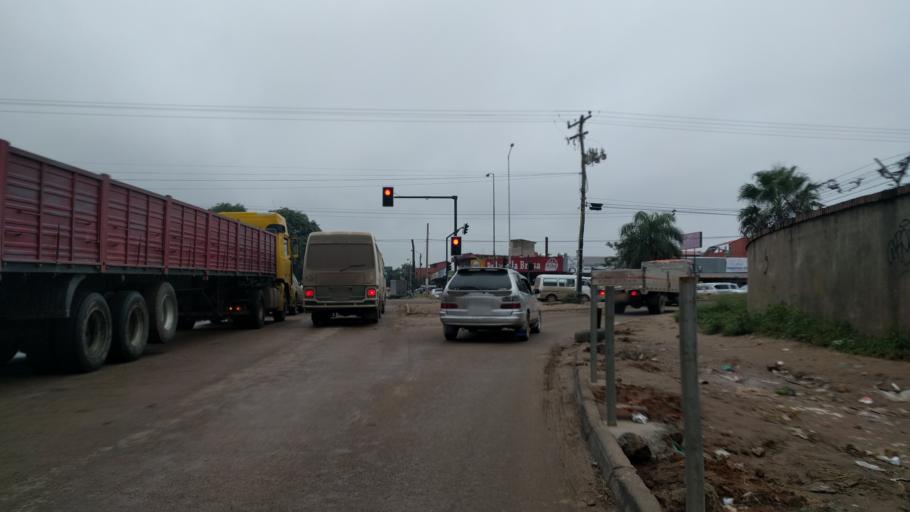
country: BO
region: Santa Cruz
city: Santa Cruz de la Sierra
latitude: -17.8167
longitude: -63.2128
